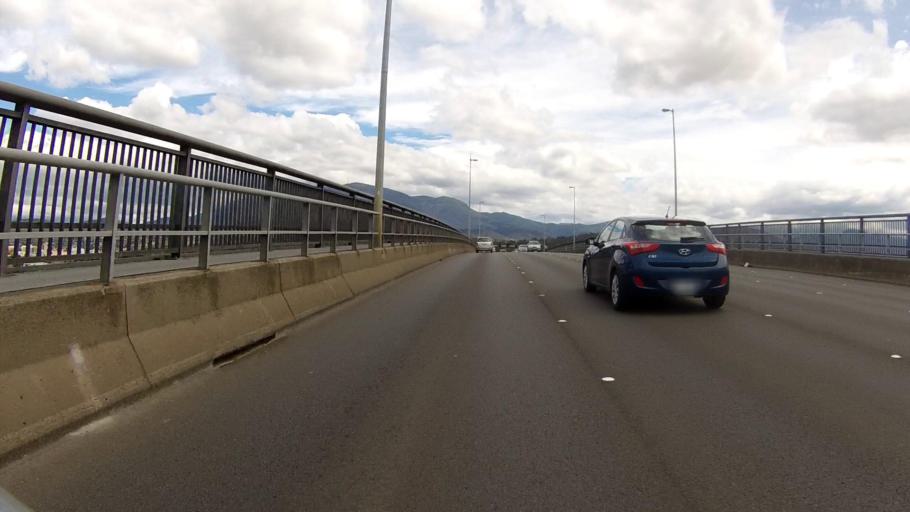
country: AU
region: Tasmania
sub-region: Clarence
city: Lindisfarne
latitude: -42.8648
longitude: 147.3502
